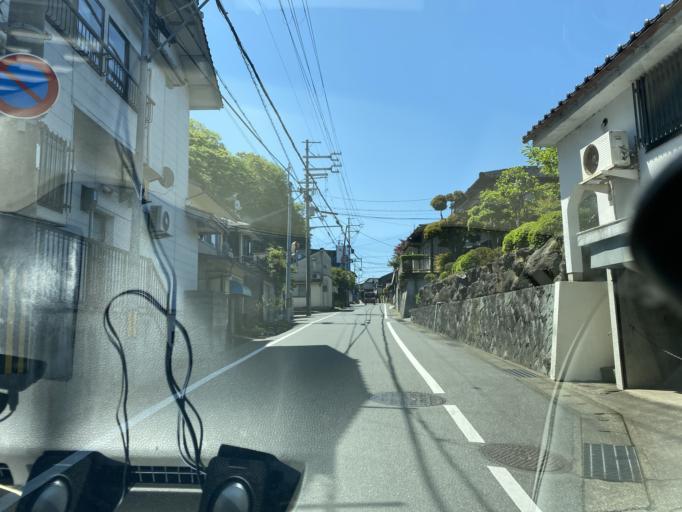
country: JP
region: Hyogo
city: Toyooka
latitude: 35.5409
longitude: 134.8196
